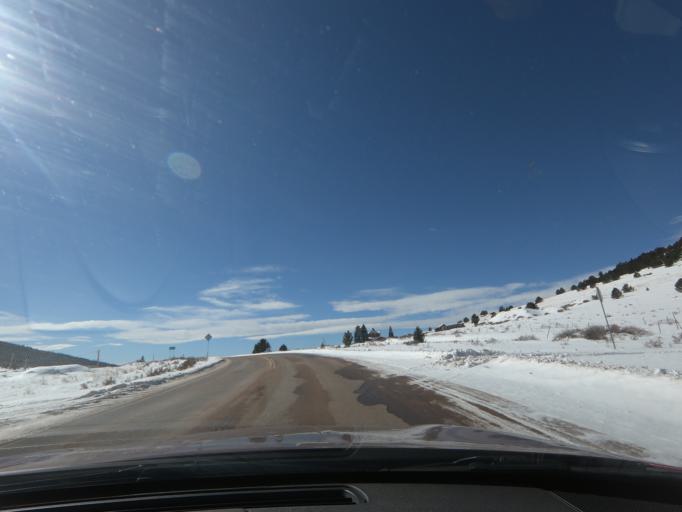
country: US
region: Colorado
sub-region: Teller County
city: Cripple Creek
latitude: 38.7313
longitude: -105.1190
